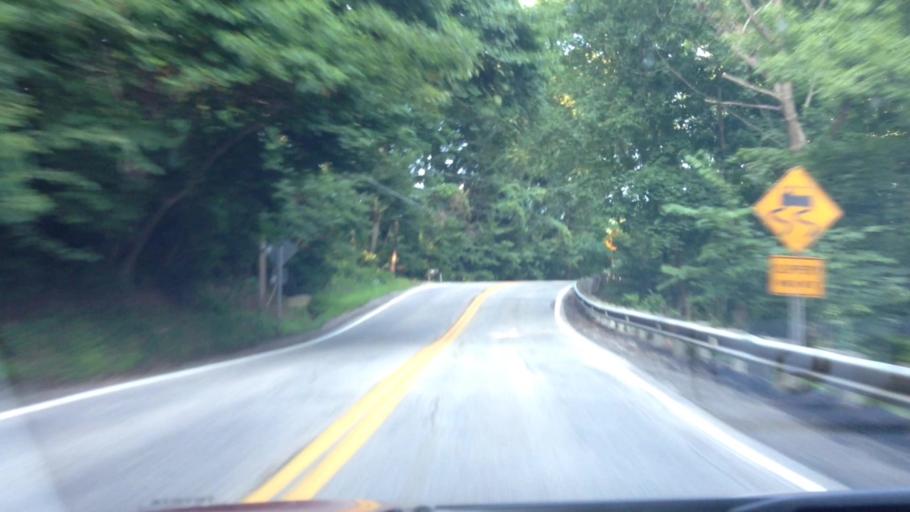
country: US
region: Ohio
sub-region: Summit County
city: Fairlawn
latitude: 41.1603
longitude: -81.6063
